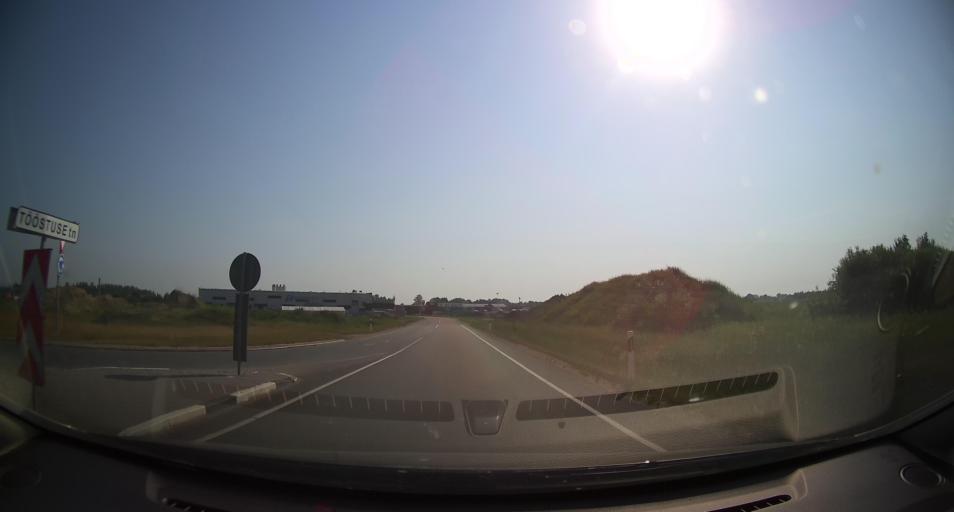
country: EE
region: Harju
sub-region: Joelaehtme vald
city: Loo
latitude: 59.3983
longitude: 24.9182
